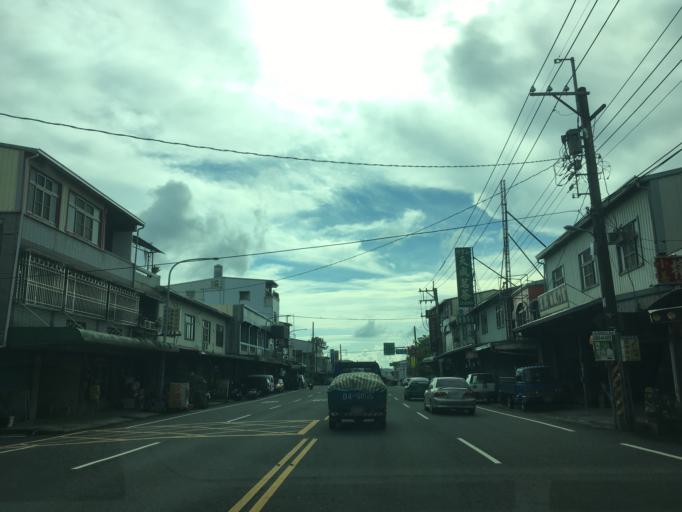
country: TW
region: Taiwan
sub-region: Chiayi
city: Jiayi Shi
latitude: 23.4412
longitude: 120.5329
